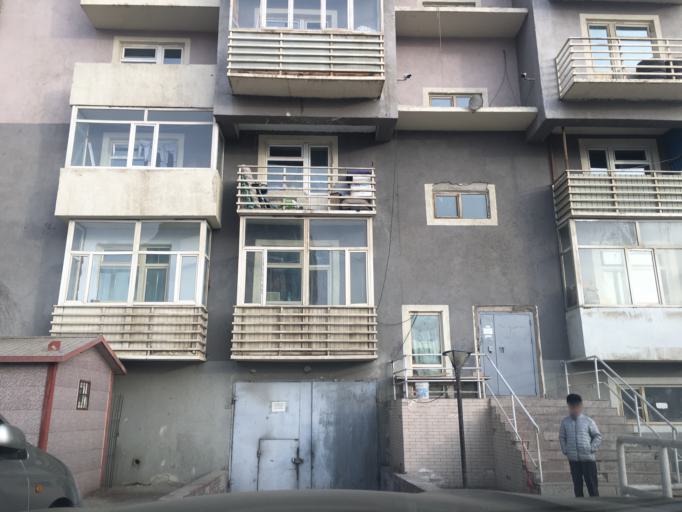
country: MN
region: Ulaanbaatar
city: Ulaanbaatar
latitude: 47.9165
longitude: 106.8866
